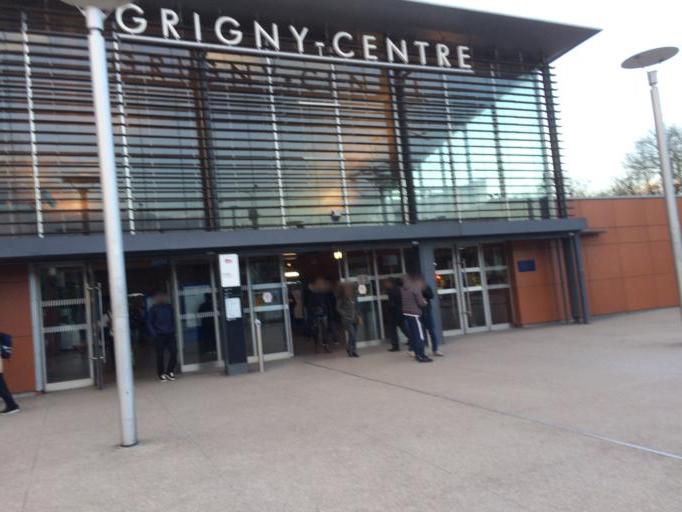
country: FR
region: Ile-de-France
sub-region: Departement de l'Essonne
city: Grigny
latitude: 48.6533
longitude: 2.3956
